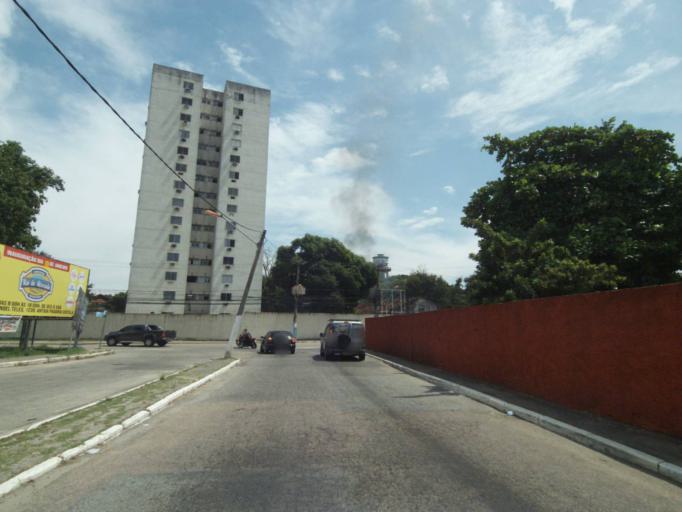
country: BR
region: Rio de Janeiro
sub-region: Duque De Caxias
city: Duque de Caxias
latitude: -22.7986
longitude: -43.3197
